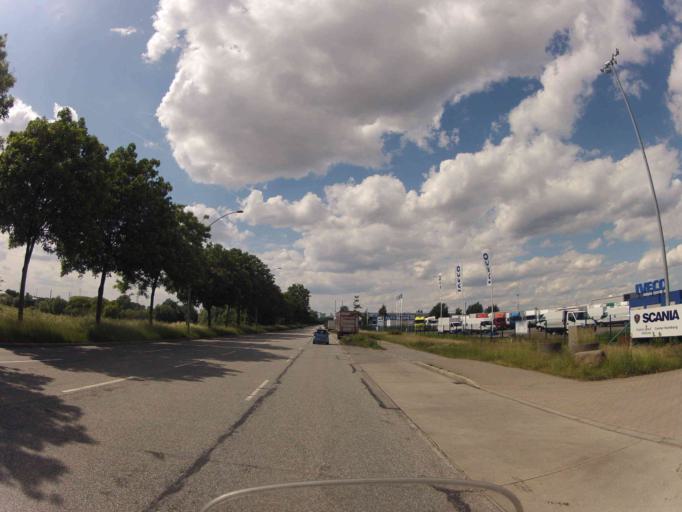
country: DE
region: Hamburg
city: Rothenburgsort
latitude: 53.5183
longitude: 10.0781
